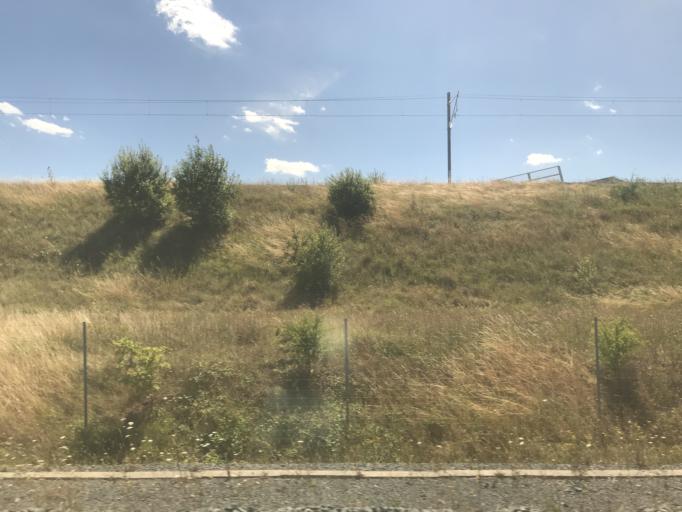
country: FR
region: Lorraine
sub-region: Departement de la Moselle
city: Remilly
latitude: 48.9586
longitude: 6.4201
